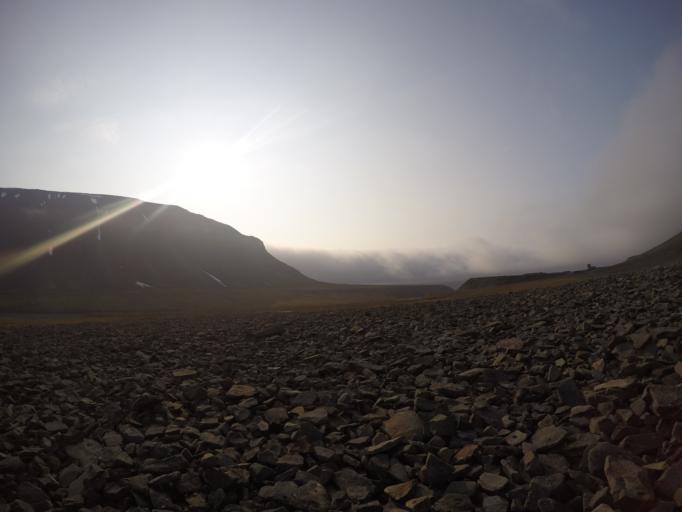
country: SJ
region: Svalbard
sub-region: Spitsbergen
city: Longyearbyen
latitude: 78.2191
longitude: 15.3369
